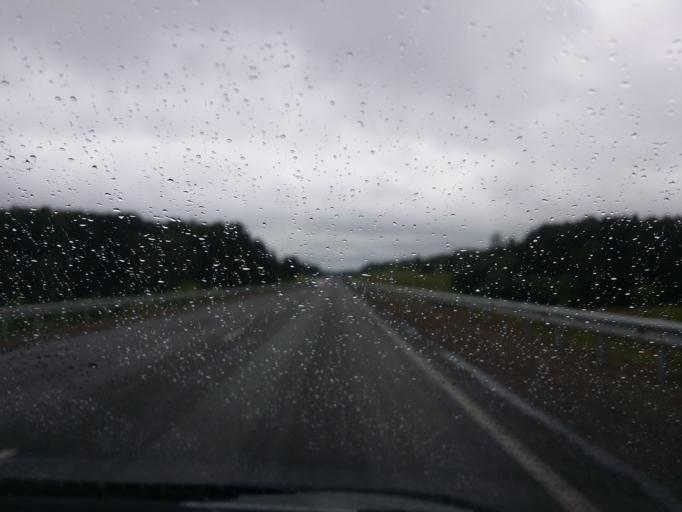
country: RU
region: Altai Krai
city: Troitskoye
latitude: 53.1137
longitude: 84.7156
